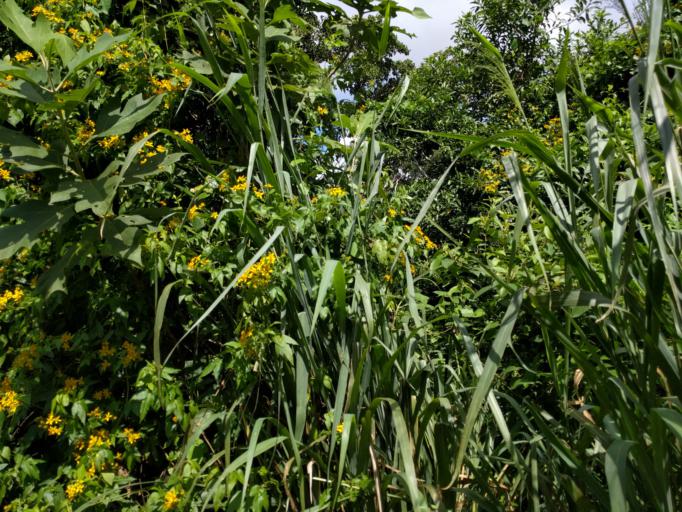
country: BO
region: Santa Cruz
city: Santa Cruz de la Sierra
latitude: -17.7983
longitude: -63.2262
